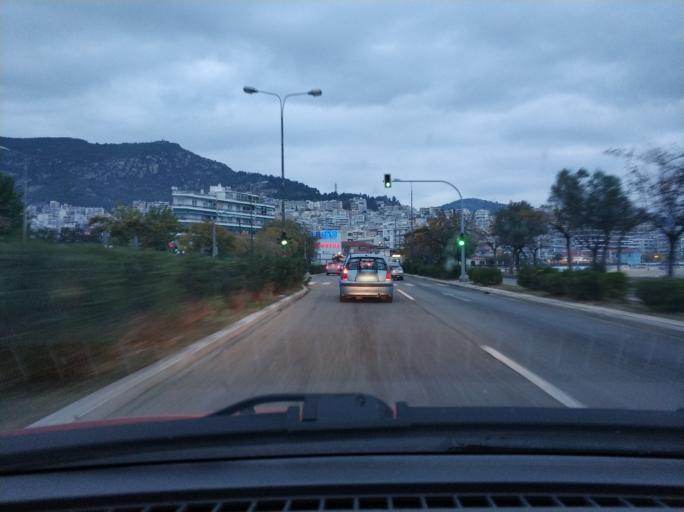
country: GR
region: East Macedonia and Thrace
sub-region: Nomos Kavalas
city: Kavala
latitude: 40.9332
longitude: 24.3935
